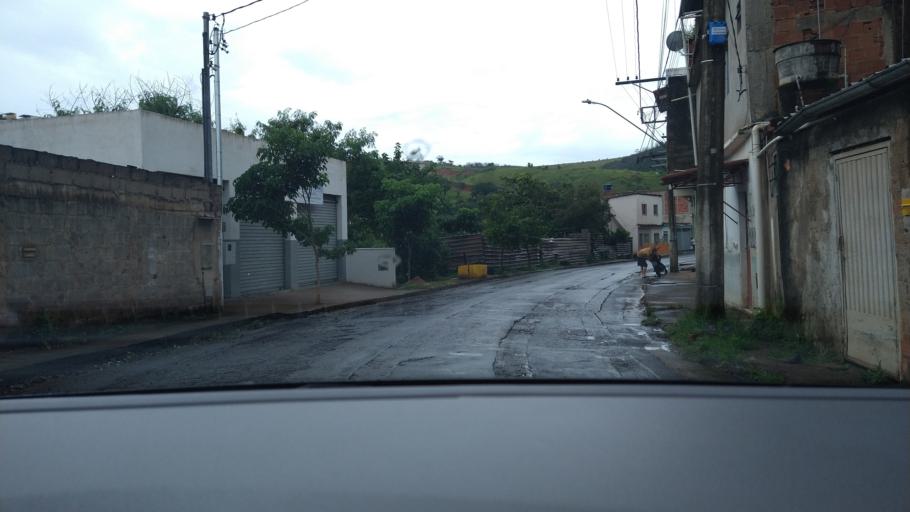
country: BR
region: Minas Gerais
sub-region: Ponte Nova
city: Ponte Nova
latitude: -20.4022
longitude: -42.9001
